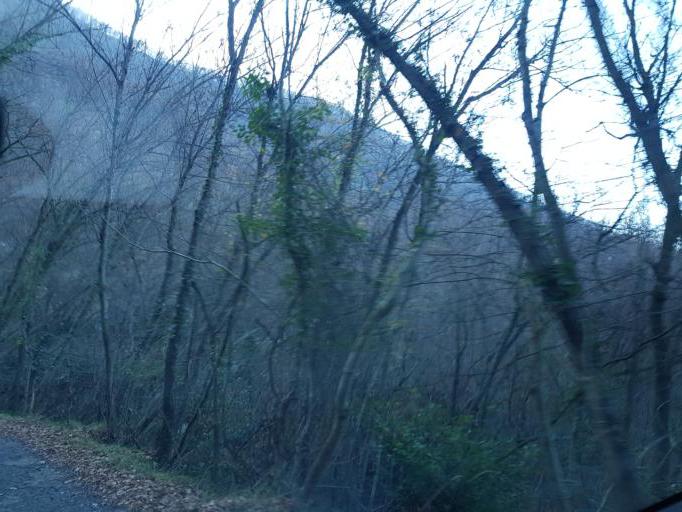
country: IT
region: Liguria
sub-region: Provincia di Genova
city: Manesseno
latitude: 44.4618
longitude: 8.9317
